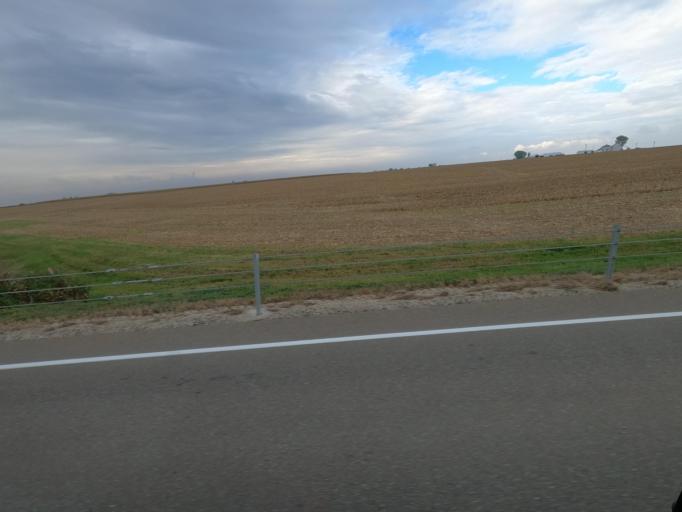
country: US
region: Iowa
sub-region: Henry County
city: Mount Pleasant
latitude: 40.7846
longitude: -91.6271
